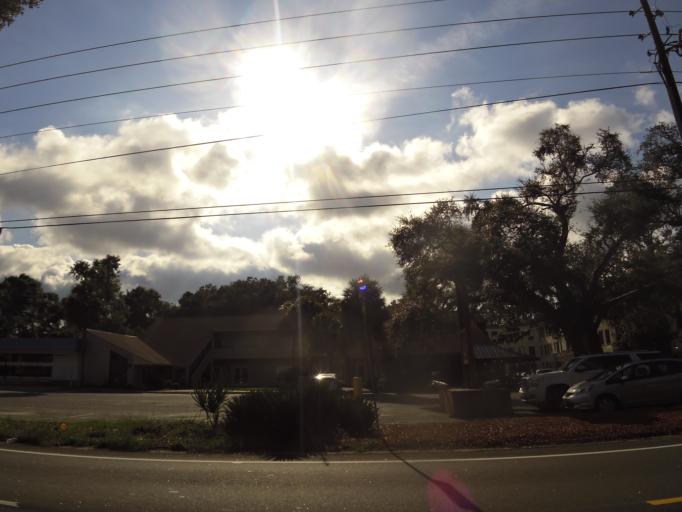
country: US
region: Georgia
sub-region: Glynn County
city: Saint Simon Mills
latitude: 31.1889
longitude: -81.3767
